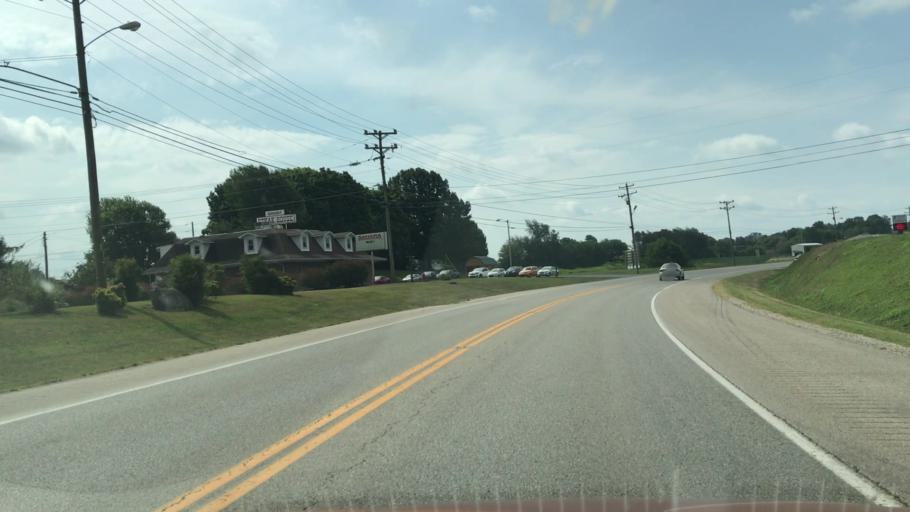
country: US
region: Kentucky
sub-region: Barren County
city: Cave City
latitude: 37.1270
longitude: -85.9619
